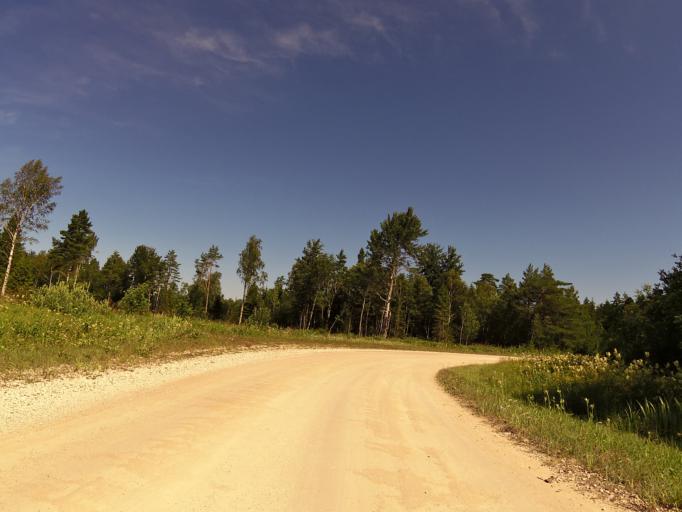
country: EE
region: Hiiumaa
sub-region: Kaerdla linn
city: Kardla
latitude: 58.9279
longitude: 22.3698
